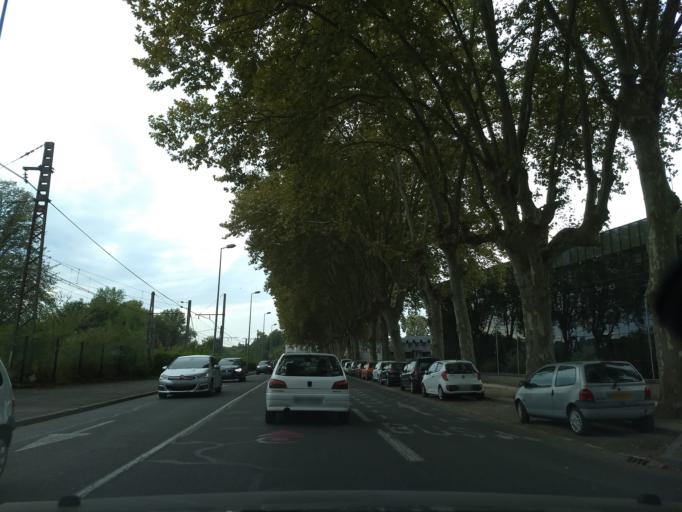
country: FR
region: Aquitaine
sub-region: Departement des Pyrenees-Atlantiques
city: Pau
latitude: 43.2927
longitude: -0.3734
